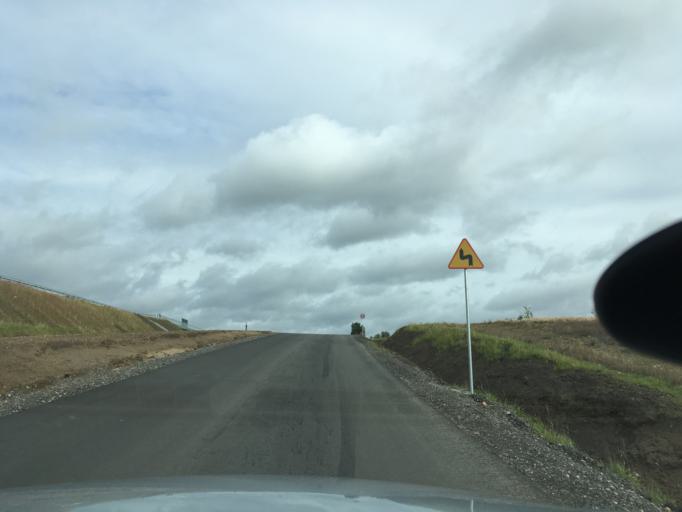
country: PL
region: Pomeranian Voivodeship
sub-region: Powiat koscierski
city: Koscierzyna
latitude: 54.1125
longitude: 18.0051
